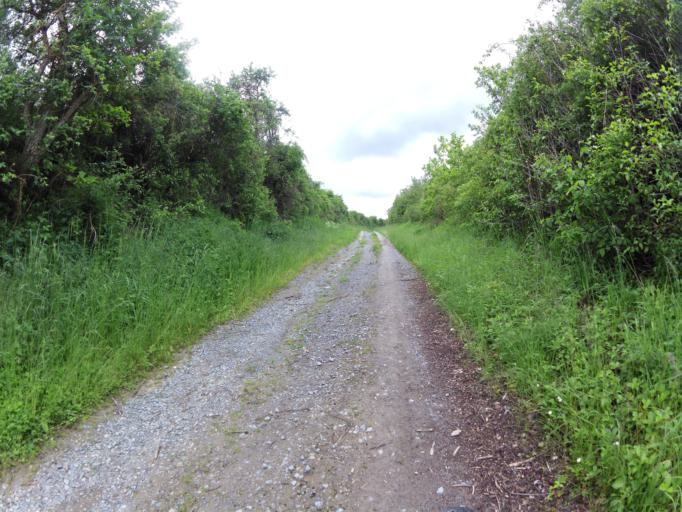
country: DE
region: Bavaria
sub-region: Regierungsbezirk Unterfranken
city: Volkach
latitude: 49.8757
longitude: 10.2198
